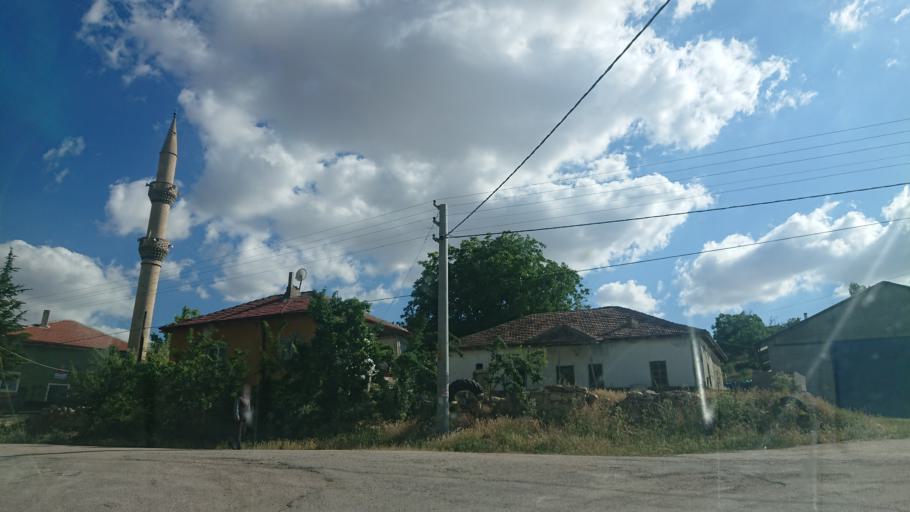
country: TR
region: Aksaray
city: Agacoren
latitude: 38.7521
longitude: 33.8874
